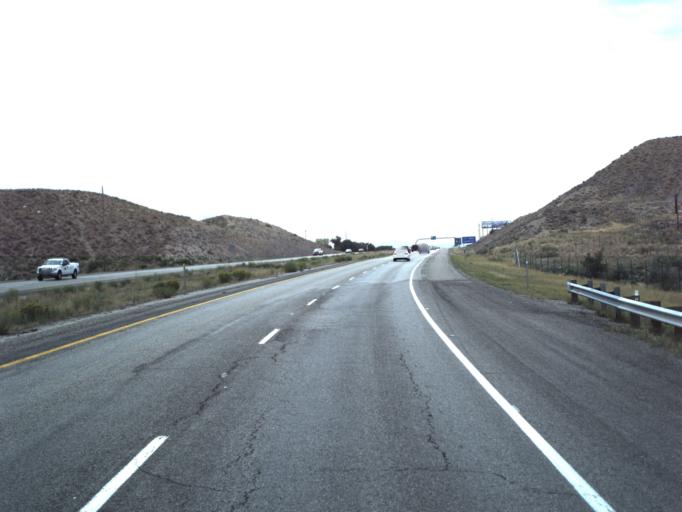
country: US
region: Utah
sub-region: Carbon County
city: Carbonville
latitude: 39.6134
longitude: -110.8377
